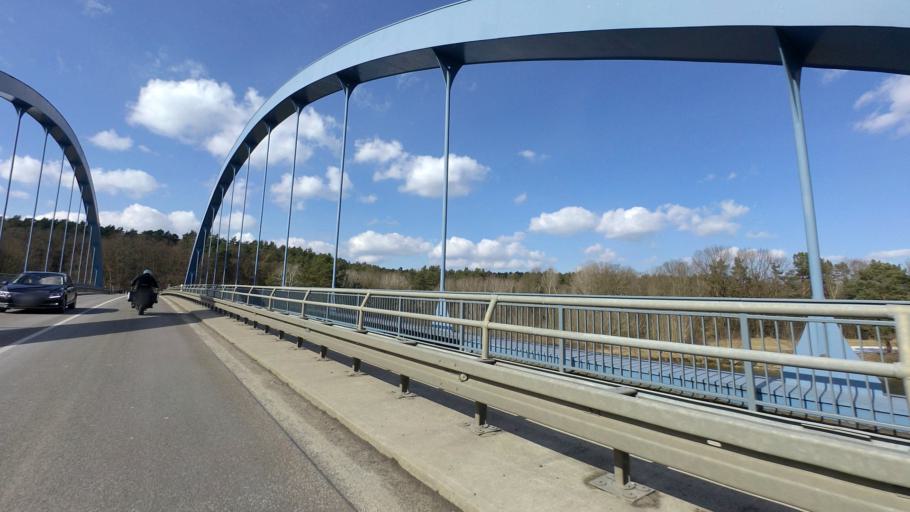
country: DE
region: Brandenburg
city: Marienwerder
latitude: 52.8550
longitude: 13.6510
